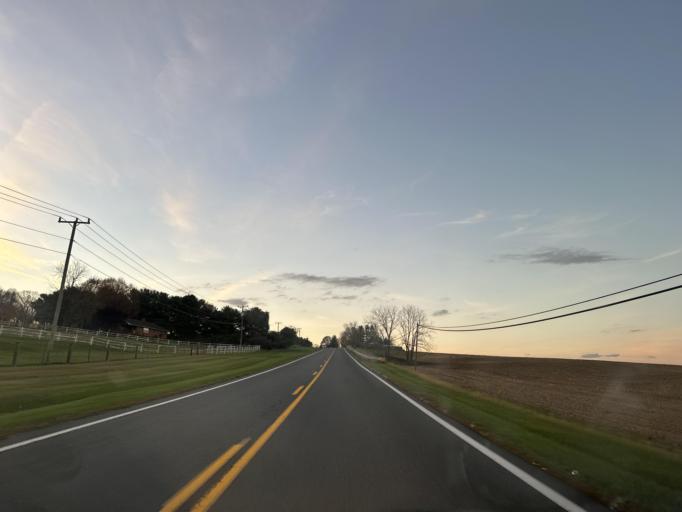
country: US
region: Virginia
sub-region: Rockingham County
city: Bridgewater
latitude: 38.4154
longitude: -78.9953
